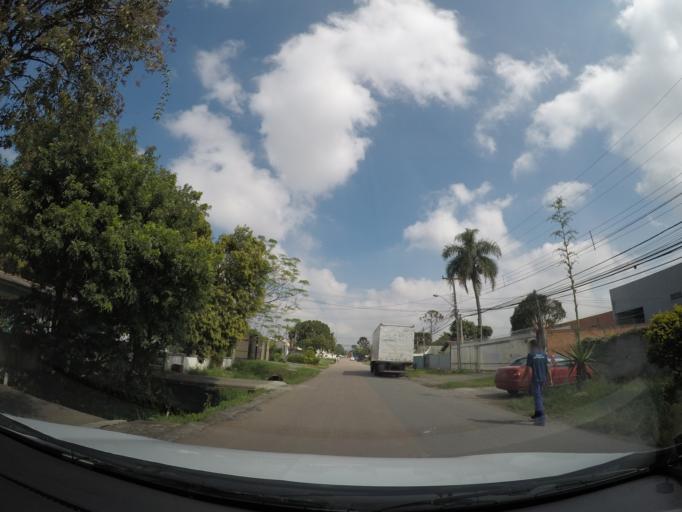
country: BR
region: Parana
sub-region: Sao Jose Dos Pinhais
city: Sao Jose dos Pinhais
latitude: -25.4953
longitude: -49.2285
